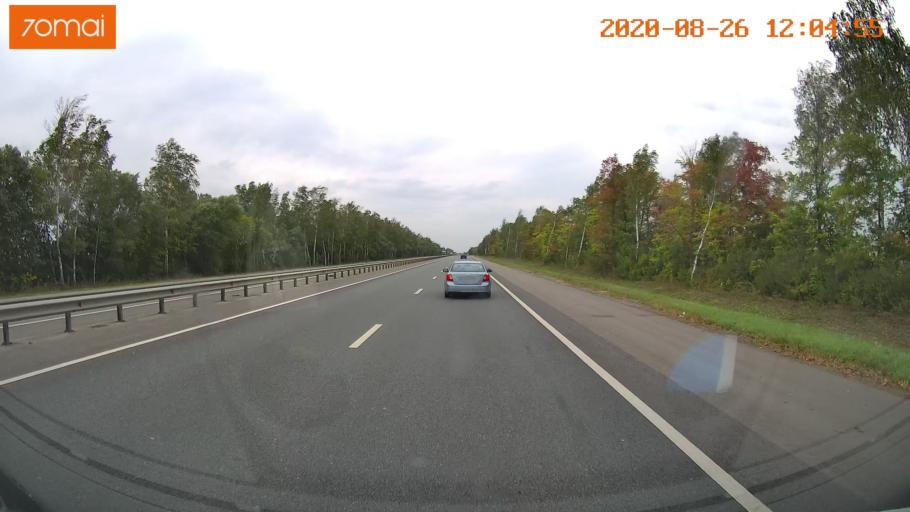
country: RU
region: Rjazan
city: Kiritsy
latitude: 54.3155
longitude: 40.1783
